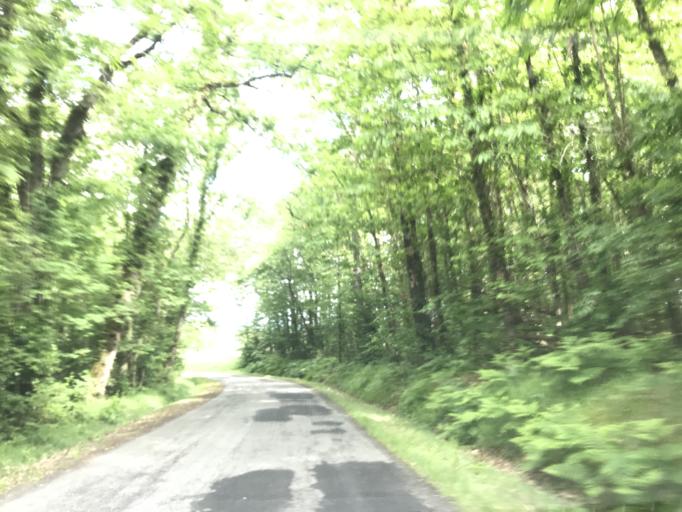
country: FR
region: Aquitaine
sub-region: Departement de la Dordogne
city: Saint-Aulaye
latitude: 45.2720
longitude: 0.1143
